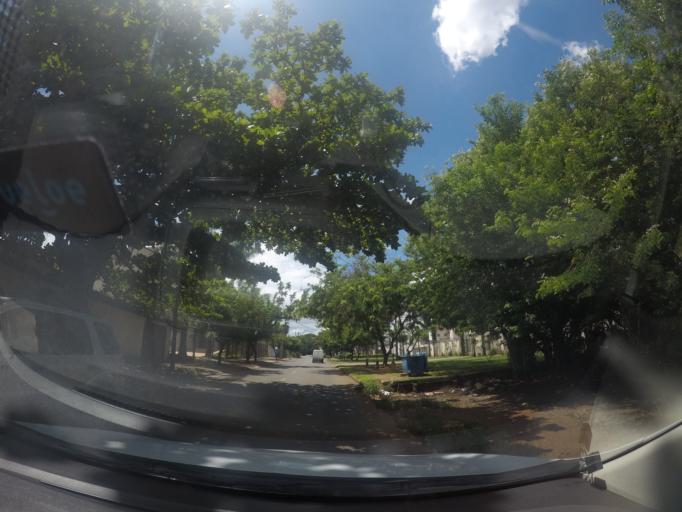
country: BR
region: Goias
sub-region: Goiania
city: Goiania
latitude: -16.7139
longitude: -49.3160
